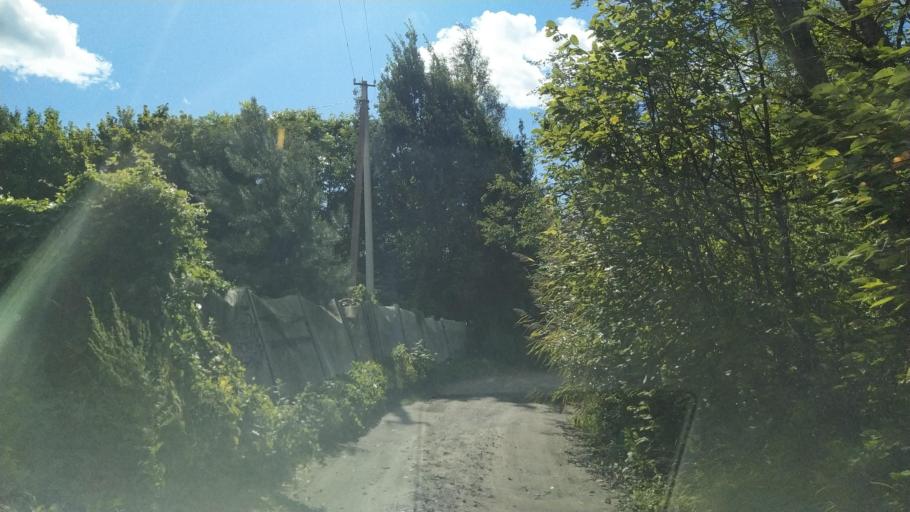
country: RU
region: Leningrad
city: Priozersk
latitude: 60.9994
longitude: 30.1703
